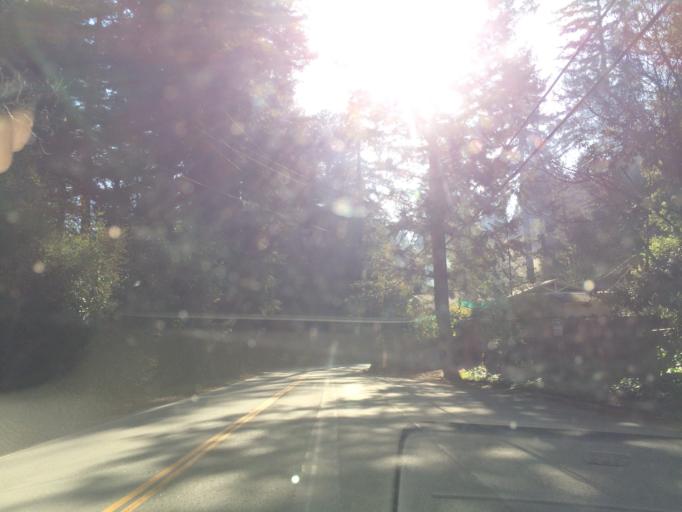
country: US
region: California
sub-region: Santa Cruz County
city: Boulder Creek
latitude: 37.1391
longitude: -122.1484
